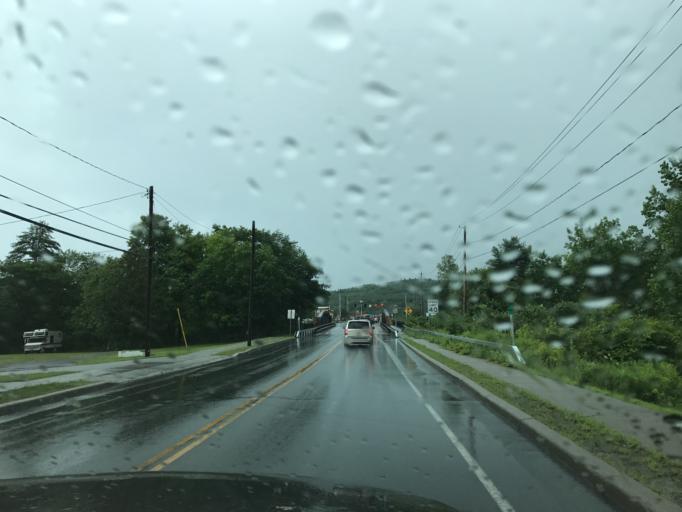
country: US
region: New York
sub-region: Warren County
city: Warrensburg
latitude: 43.4885
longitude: -73.7619
